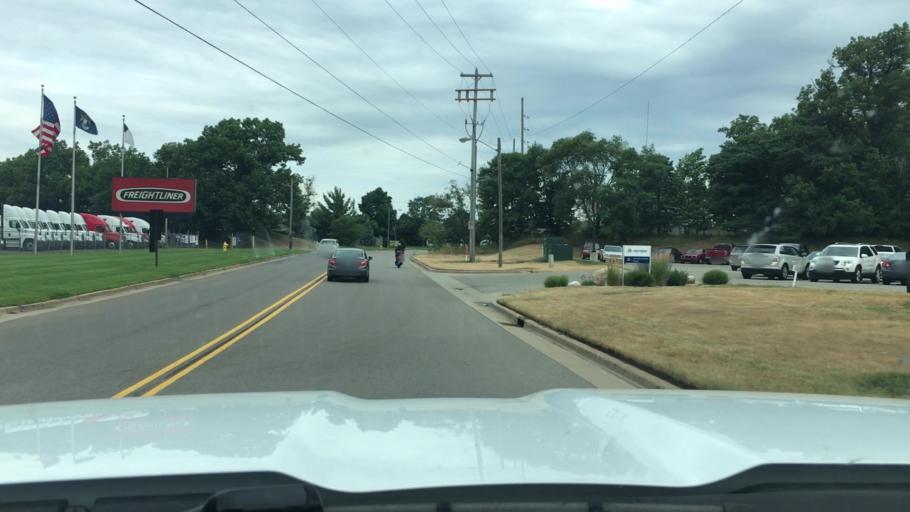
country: US
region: Michigan
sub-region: Kent County
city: Cutlerville
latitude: 42.8689
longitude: -85.6763
